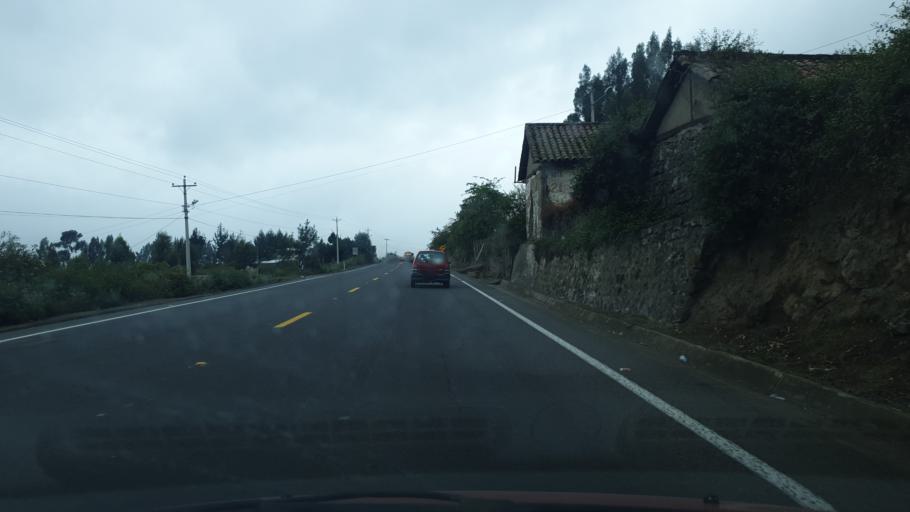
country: EC
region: Tungurahua
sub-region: Canton Quero
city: Quero
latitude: -1.3811
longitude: -78.6480
